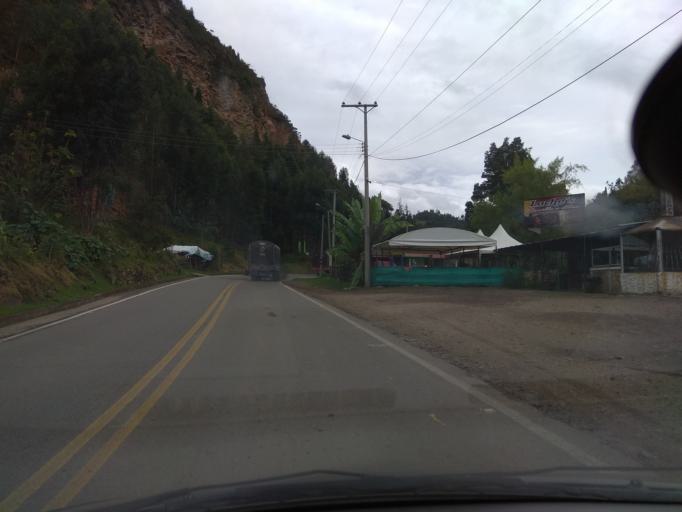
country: CO
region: Boyaca
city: Duitama
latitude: 5.8413
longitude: -73.0149
